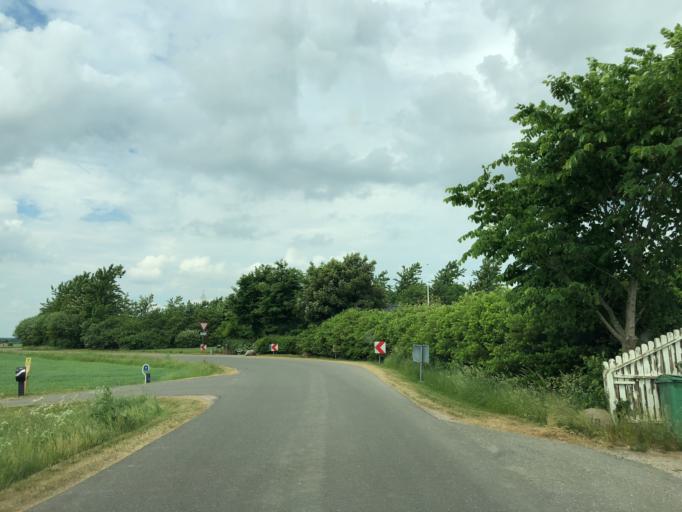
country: DK
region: Central Jutland
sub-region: Struer Kommune
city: Struer
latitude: 56.4677
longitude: 8.5612
